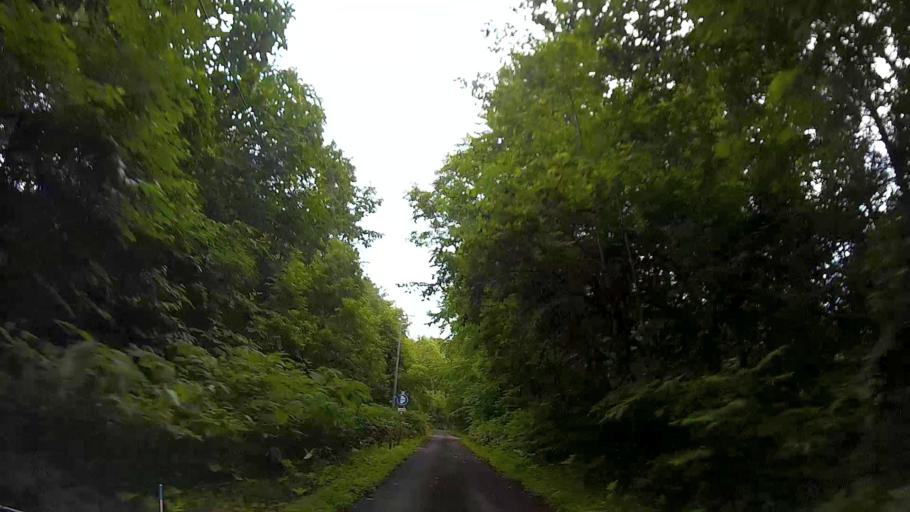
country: JP
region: Hokkaido
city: Nanae
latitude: 42.1041
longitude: 140.4525
